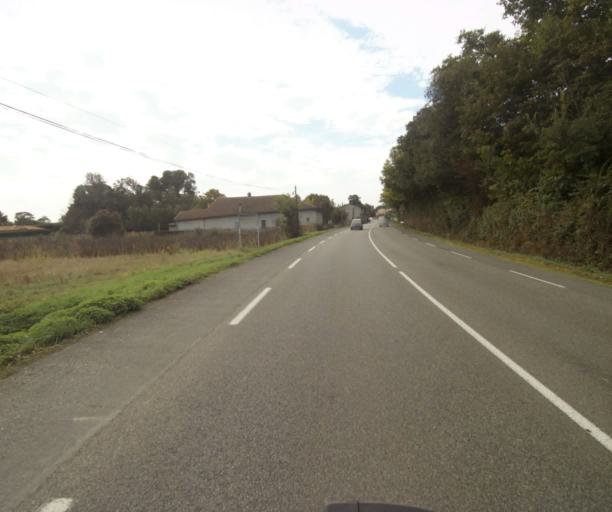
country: FR
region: Midi-Pyrenees
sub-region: Departement du Tarn-et-Garonne
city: Finhan
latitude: 43.9164
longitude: 1.2249
